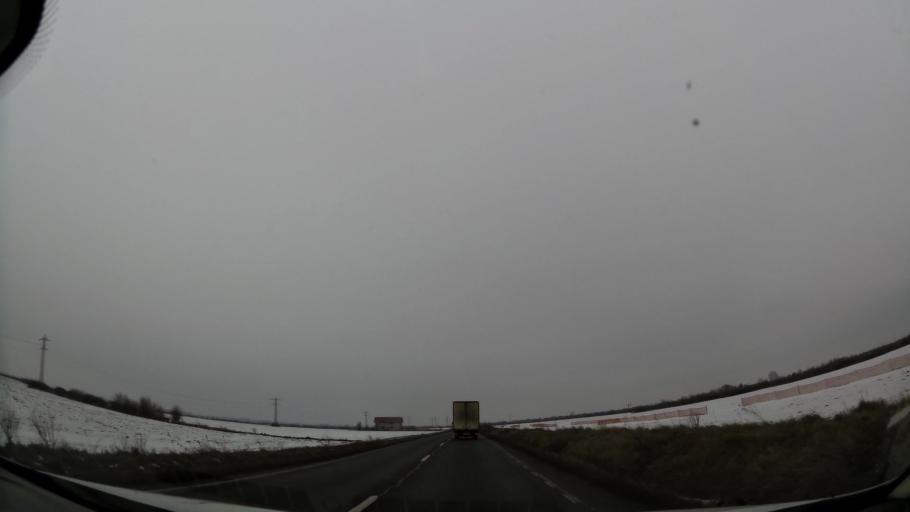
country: RO
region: Dambovita
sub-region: Comuna Racari
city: Mavrodin
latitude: 44.6412
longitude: 25.7084
